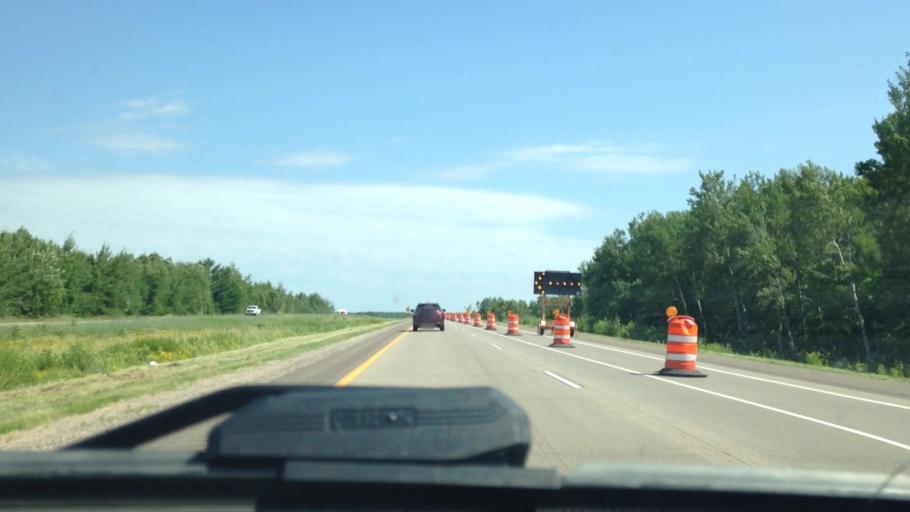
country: US
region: Wisconsin
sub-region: Barron County
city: Rice Lake
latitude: 45.5702
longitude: -91.7629
